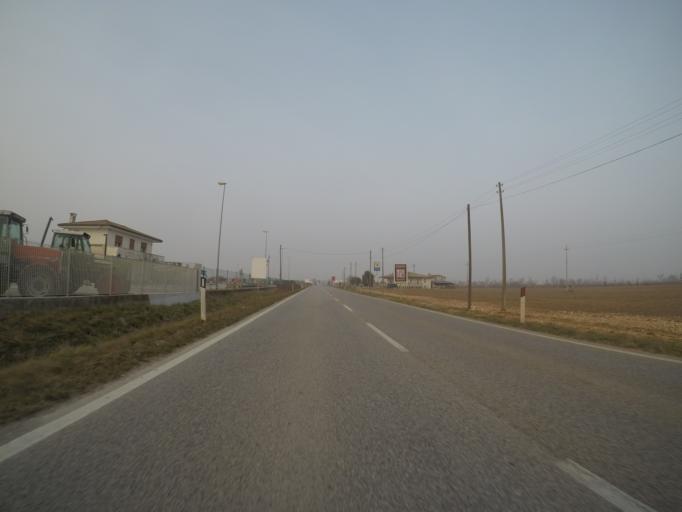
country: IT
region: Veneto
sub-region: Provincia di Treviso
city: Altivole
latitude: 45.7280
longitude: 11.9552
